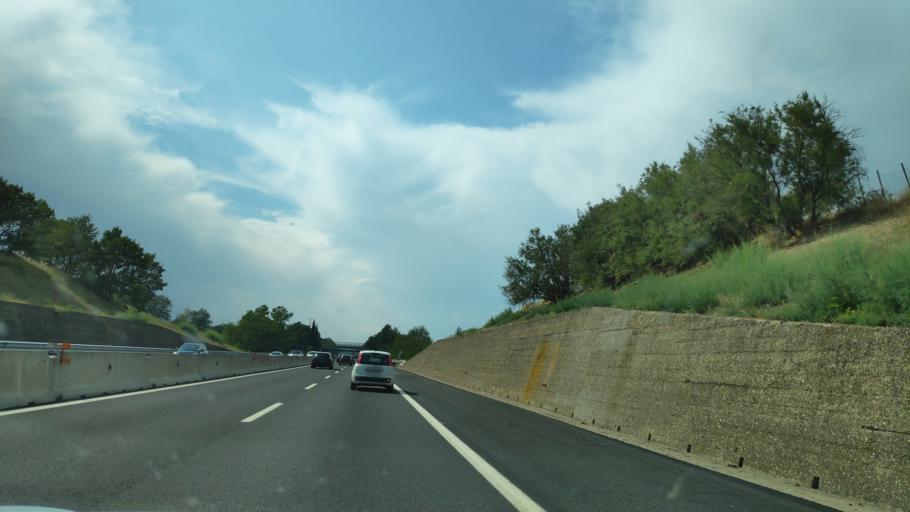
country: IT
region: Tuscany
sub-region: Province of Arezzo
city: Ponticino
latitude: 43.4856
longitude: 11.7019
